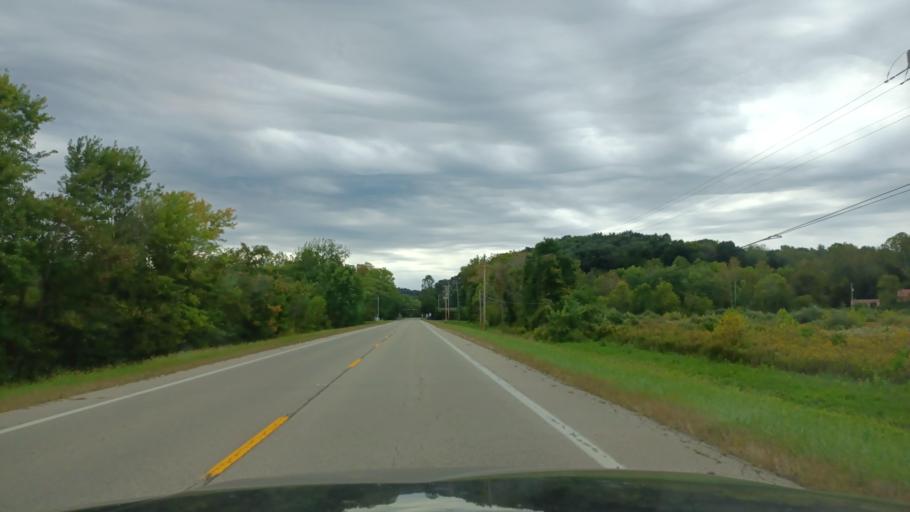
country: US
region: Ohio
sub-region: Vinton County
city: McArthur
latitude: 39.2348
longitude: -82.4312
